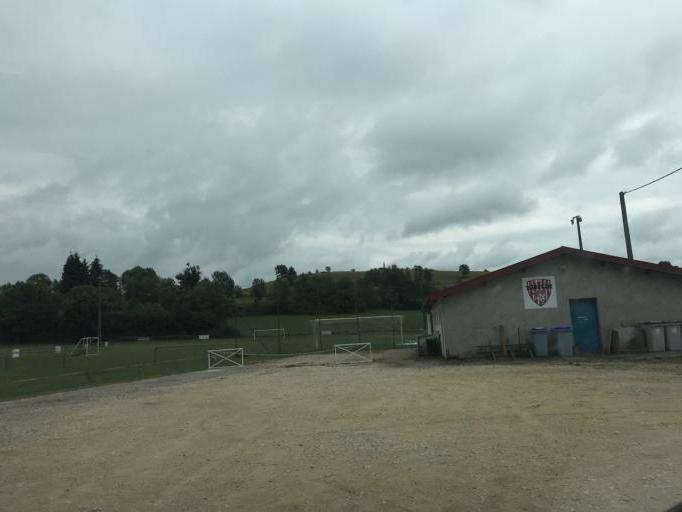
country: FR
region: Rhone-Alpes
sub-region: Departement de l'Ain
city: Arbent
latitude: 46.3070
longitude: 5.7388
